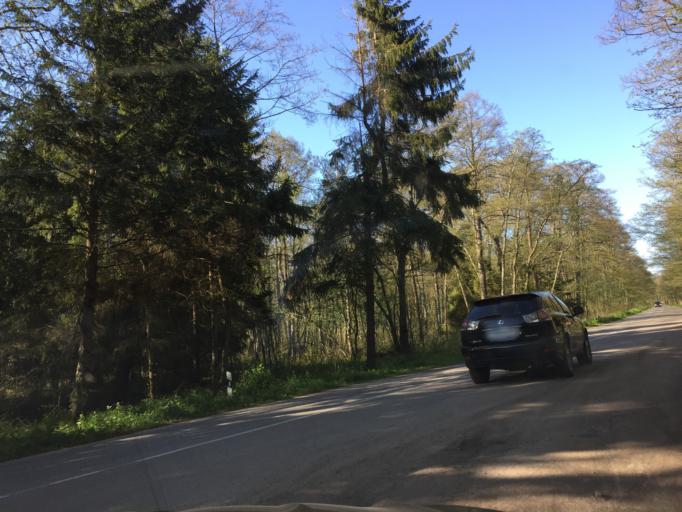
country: LT
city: Nida
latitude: 55.1841
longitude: 20.8548
